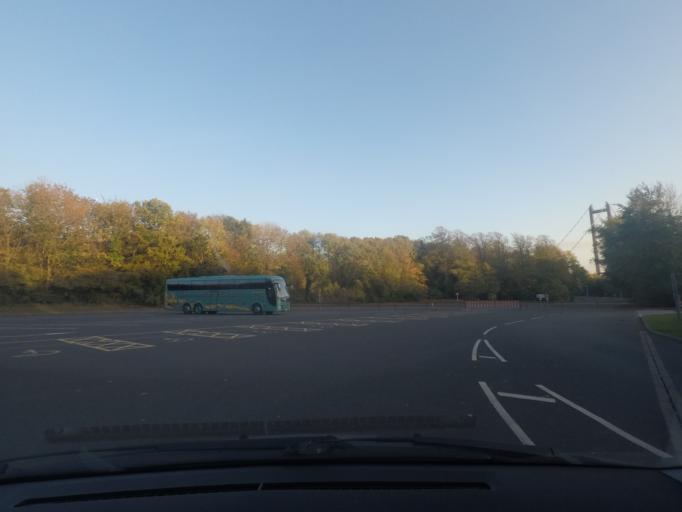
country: GB
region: England
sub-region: East Riding of Yorkshire
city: Hessle
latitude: 53.7200
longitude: -0.4533
